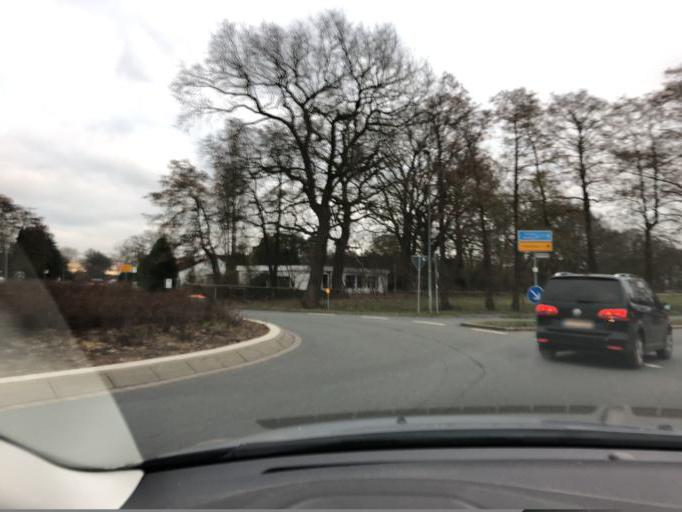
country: DE
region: Lower Saxony
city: Ganderkesee
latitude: 53.0660
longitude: 8.5752
